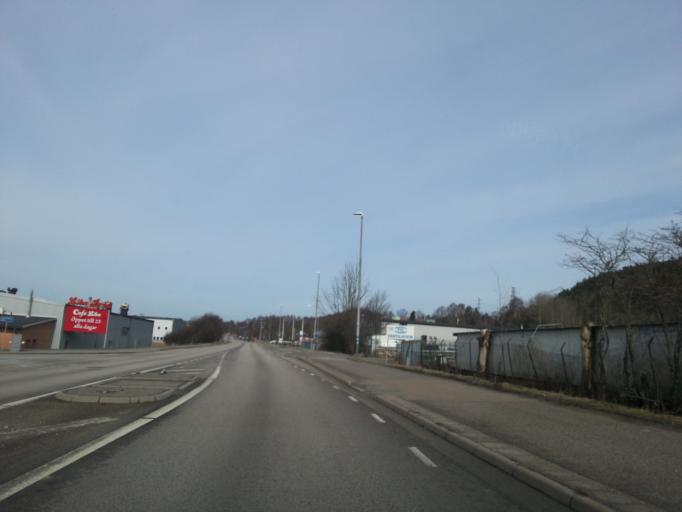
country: SE
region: Vaestra Goetaland
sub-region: Goteborg
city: Eriksbo
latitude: 57.7527
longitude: 12.0113
